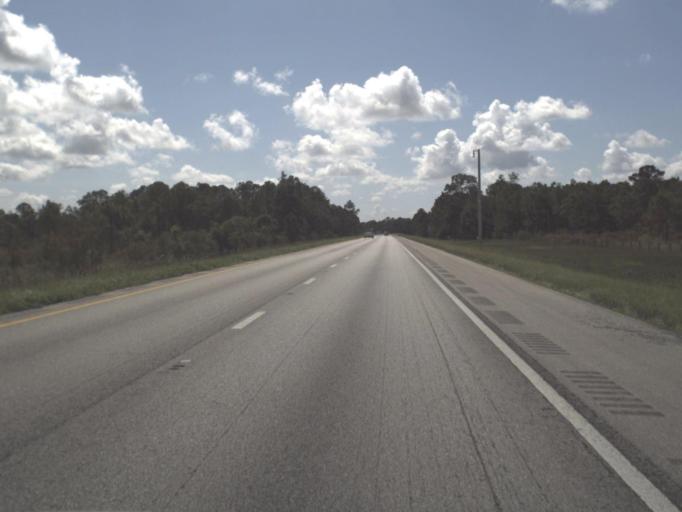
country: US
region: Florida
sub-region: Lee County
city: Suncoast Estates
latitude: 26.7876
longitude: -81.9033
